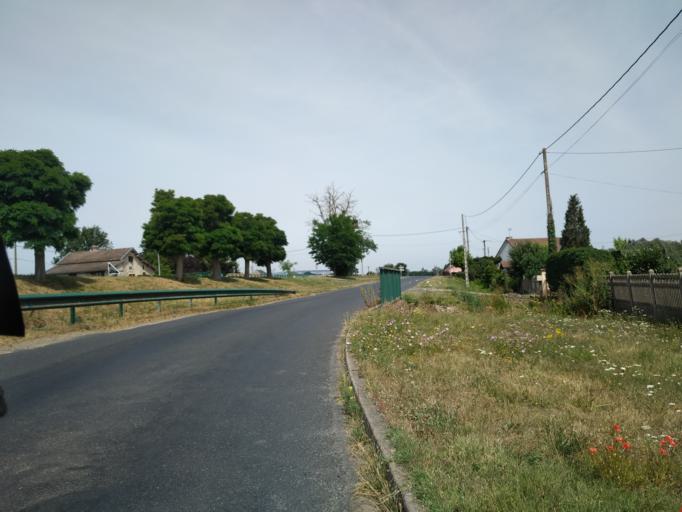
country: FR
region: Auvergne
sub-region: Departement de l'Allier
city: Molinet
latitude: 46.4520
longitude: 3.9672
